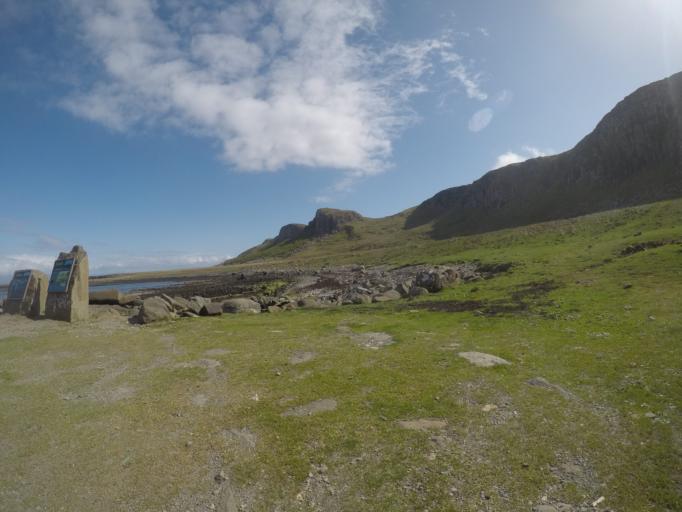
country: GB
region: Scotland
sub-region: Highland
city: Portree
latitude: 57.6330
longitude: -6.1984
